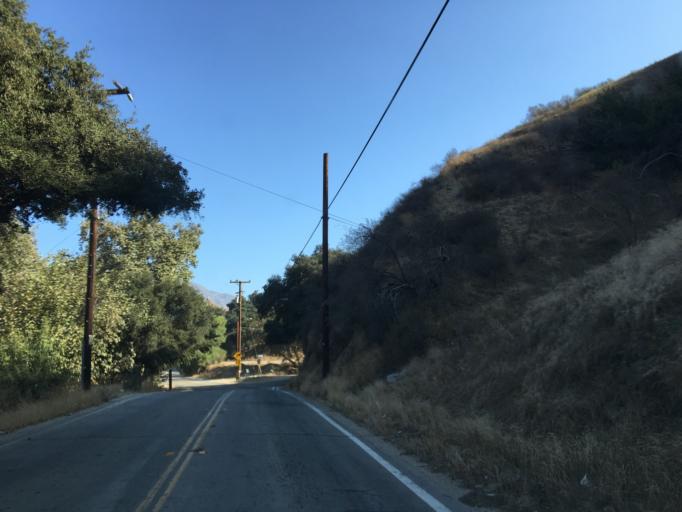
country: US
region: California
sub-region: Los Angeles County
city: San Fernando
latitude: 34.2940
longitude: -118.3997
